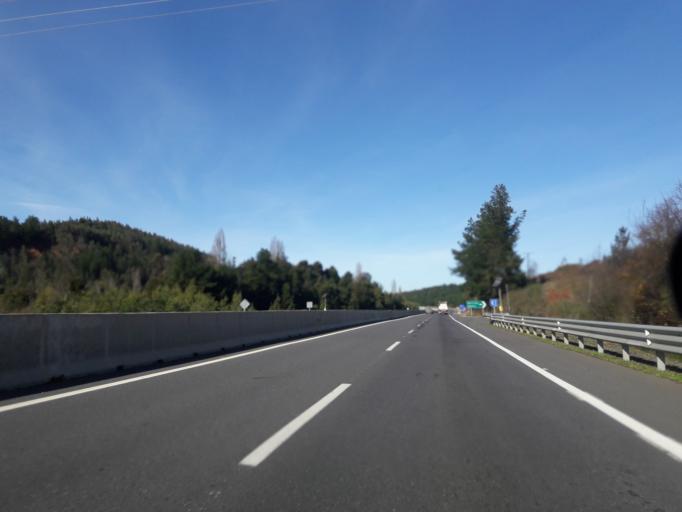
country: CL
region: Biobio
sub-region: Provincia de Biobio
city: Yumbel
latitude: -36.9530
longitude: -72.7471
